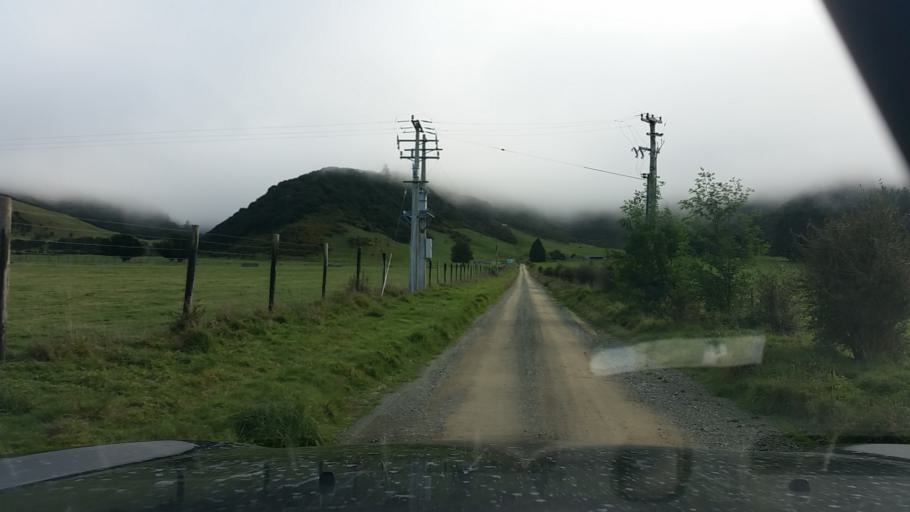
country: NZ
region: Marlborough
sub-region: Marlborough District
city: Picton
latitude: -41.1724
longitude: 173.9665
